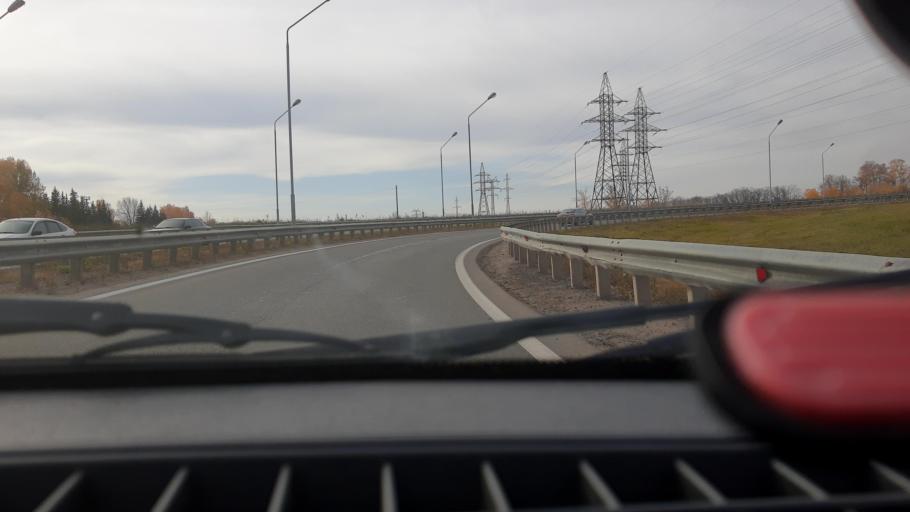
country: RU
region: Bashkortostan
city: Avdon
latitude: 54.6756
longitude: 55.8024
